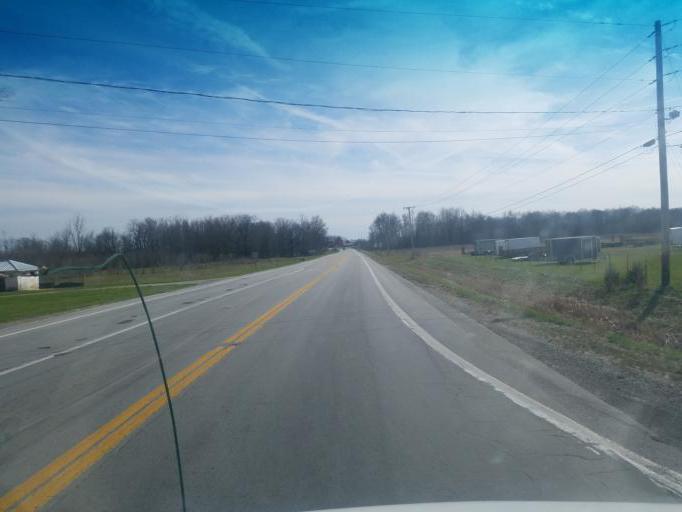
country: US
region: Ohio
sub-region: Union County
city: Richwood
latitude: 40.3944
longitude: -83.2703
